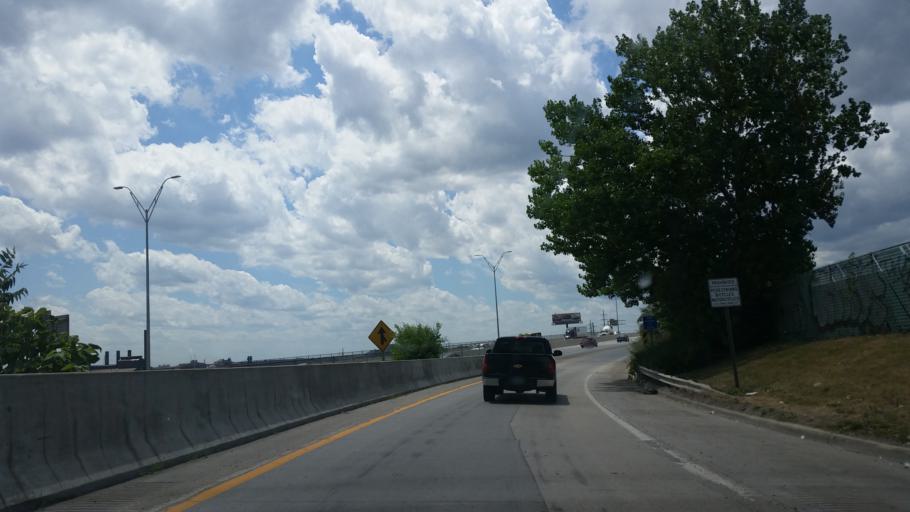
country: US
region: Ohio
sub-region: Cuyahoga County
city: Newburgh Heights
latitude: 41.4802
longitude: -81.6677
